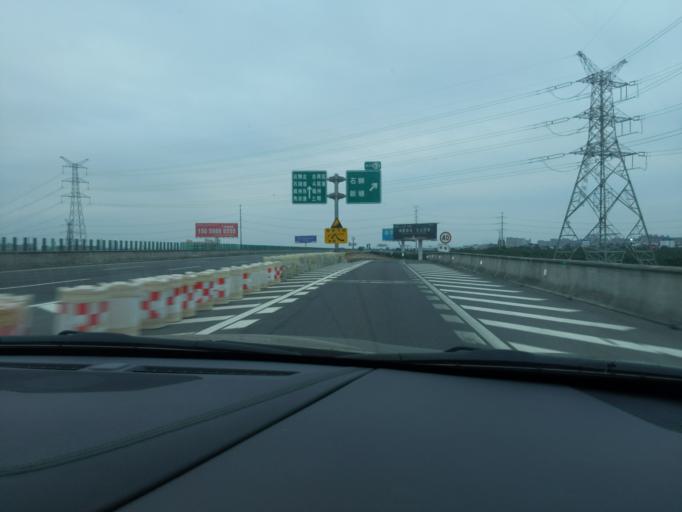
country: CN
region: Fujian
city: Xibin
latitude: 24.7721
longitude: 118.6225
